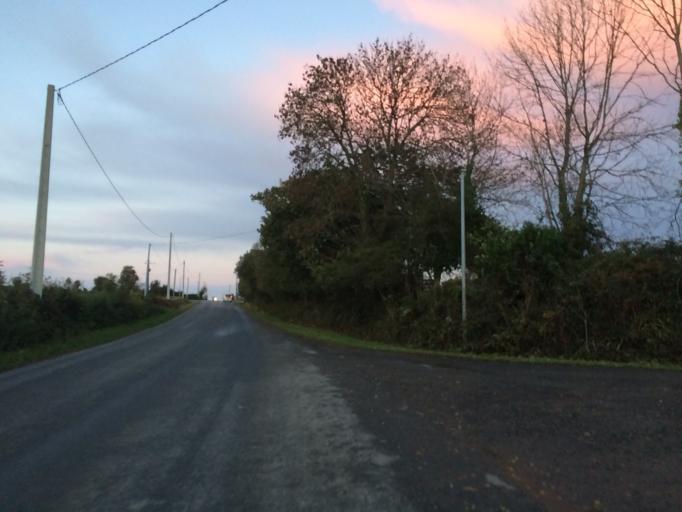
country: FR
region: Brittany
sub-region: Departement du Finistere
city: Hopital-Camfrout
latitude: 48.3499
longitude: -4.2311
